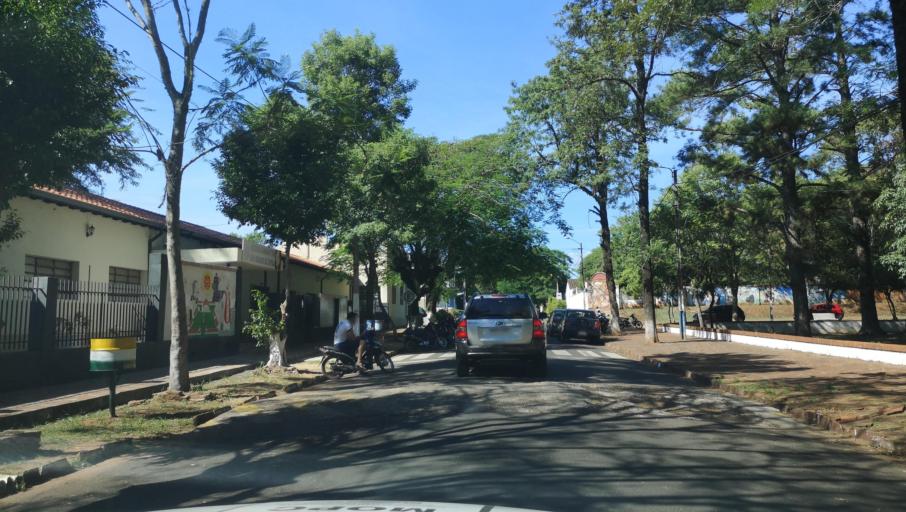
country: PY
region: Misiones
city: Santa Maria
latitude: -26.8893
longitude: -57.0233
